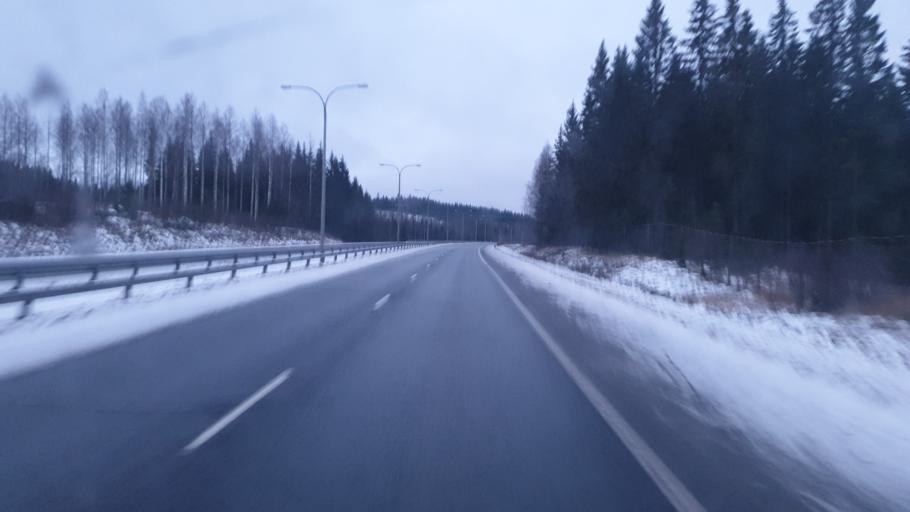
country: FI
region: Northern Savo
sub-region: Kuopio
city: Siilinjaervi
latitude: 63.0448
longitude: 27.6628
